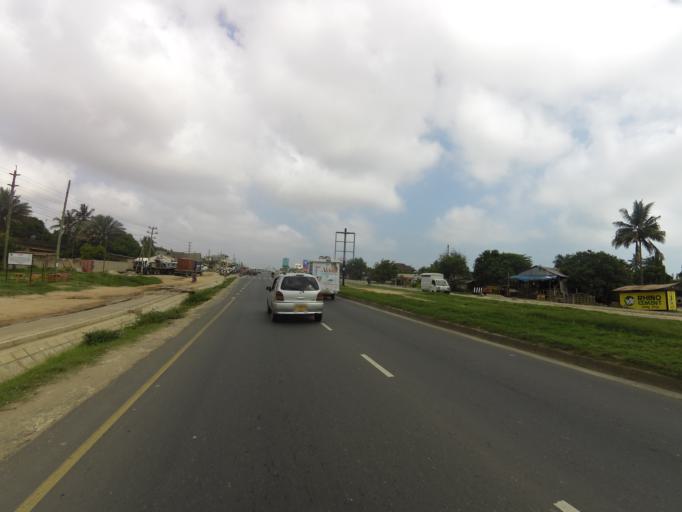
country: TZ
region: Dar es Salaam
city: Magomeni
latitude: -6.7186
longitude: 39.2117
